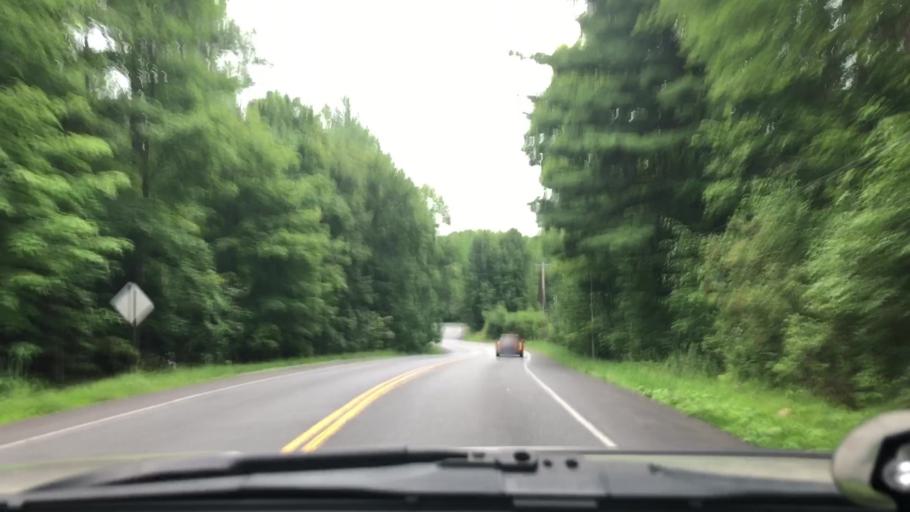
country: US
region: New York
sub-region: Saratoga County
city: Corinth
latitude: 43.2074
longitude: -73.7738
